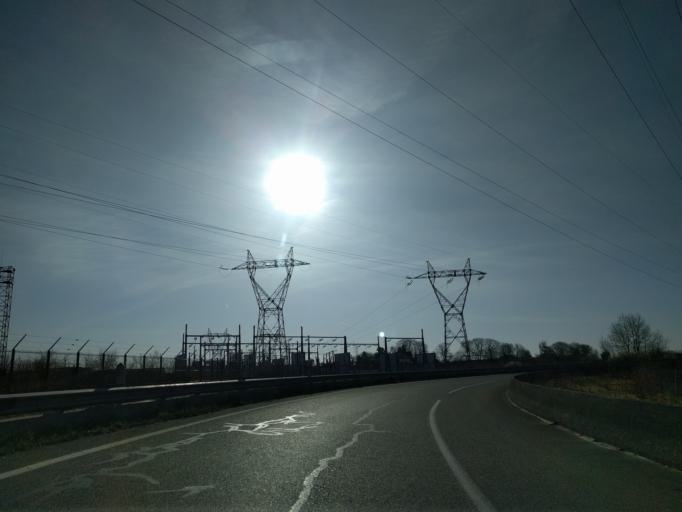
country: FR
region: Ile-de-France
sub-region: Departement de Seine-et-Marne
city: Moissy-Cramayel
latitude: 48.6090
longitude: 2.5825
